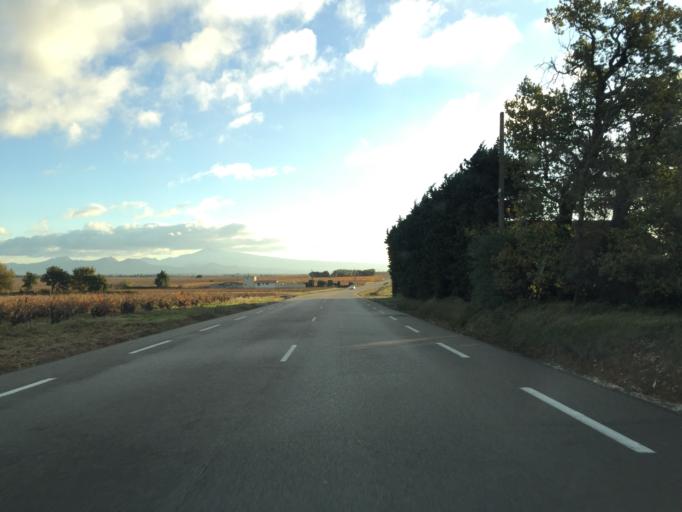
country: FR
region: Provence-Alpes-Cote d'Azur
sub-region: Departement du Vaucluse
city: Chateauneuf-du-Pape
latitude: 44.0961
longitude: 4.8284
